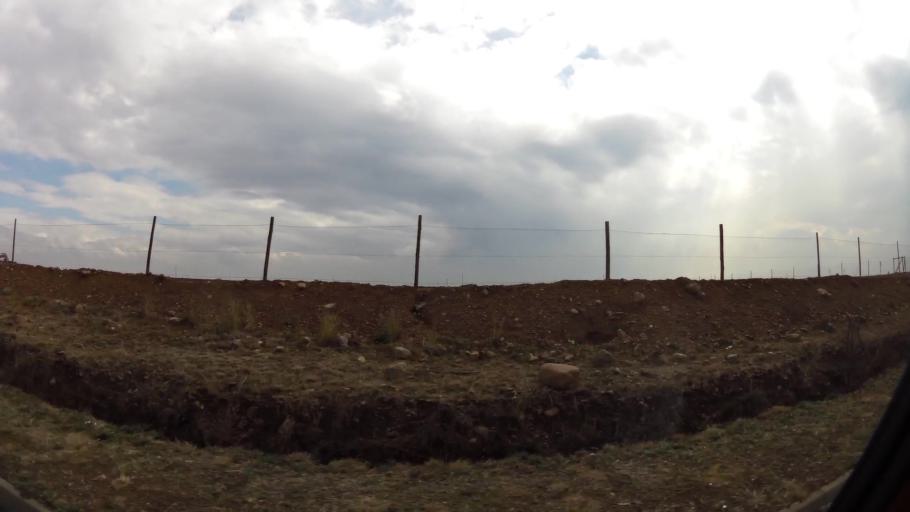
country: ZA
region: Gauteng
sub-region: Sedibeng District Municipality
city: Vanderbijlpark
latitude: -26.7212
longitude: 27.8821
